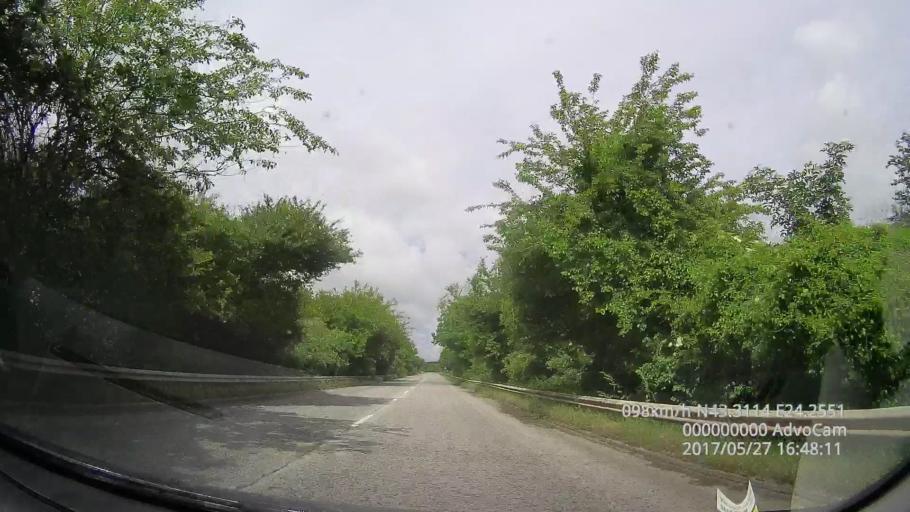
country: BG
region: Pleven
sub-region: Obshtina Cherven Bryag
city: Koynare
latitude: 43.3120
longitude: 24.2560
